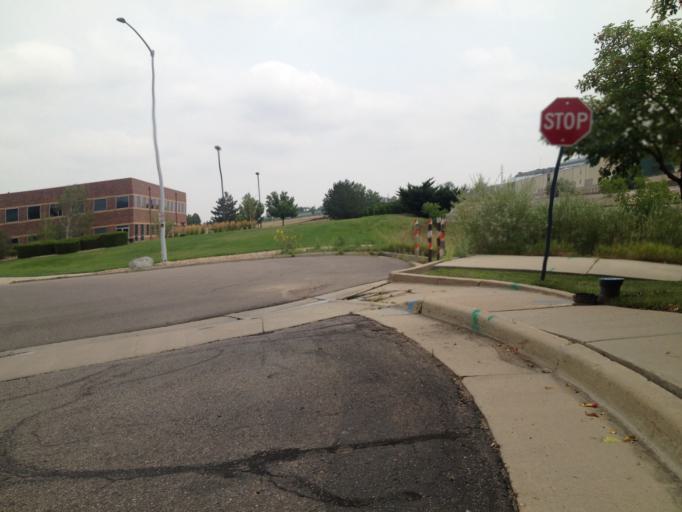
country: US
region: Colorado
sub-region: Broomfield County
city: Broomfield
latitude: 39.9263
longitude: -105.1090
